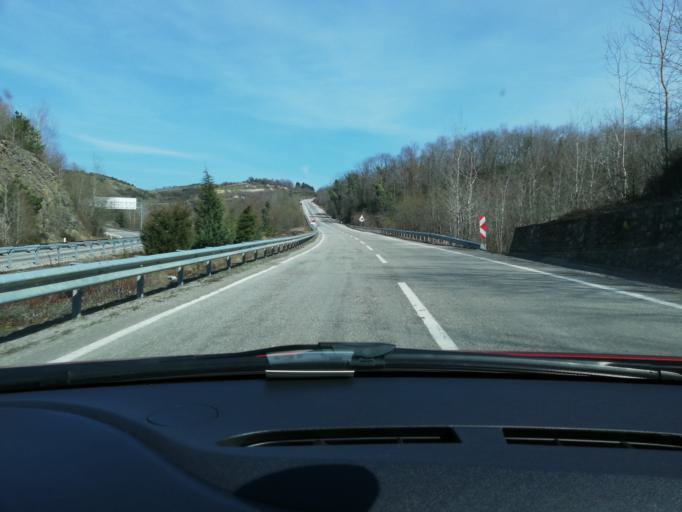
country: TR
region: Bartin
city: Amasra
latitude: 41.7235
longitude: 32.4025
